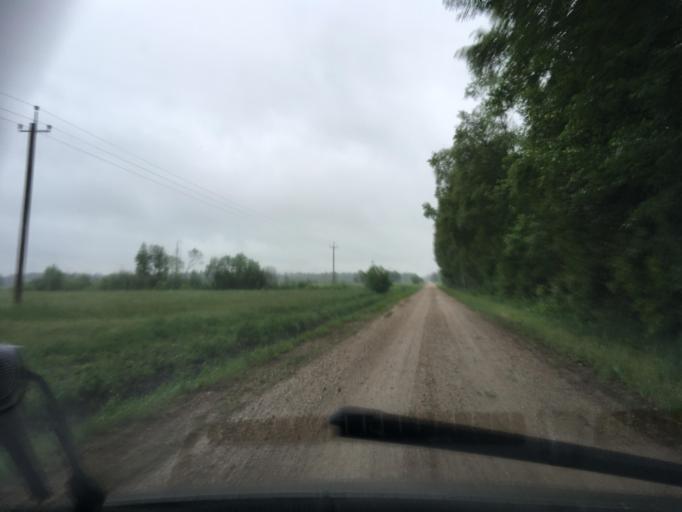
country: EE
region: Laeaene
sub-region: Lihula vald
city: Lihula
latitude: 58.6078
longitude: 23.8286
